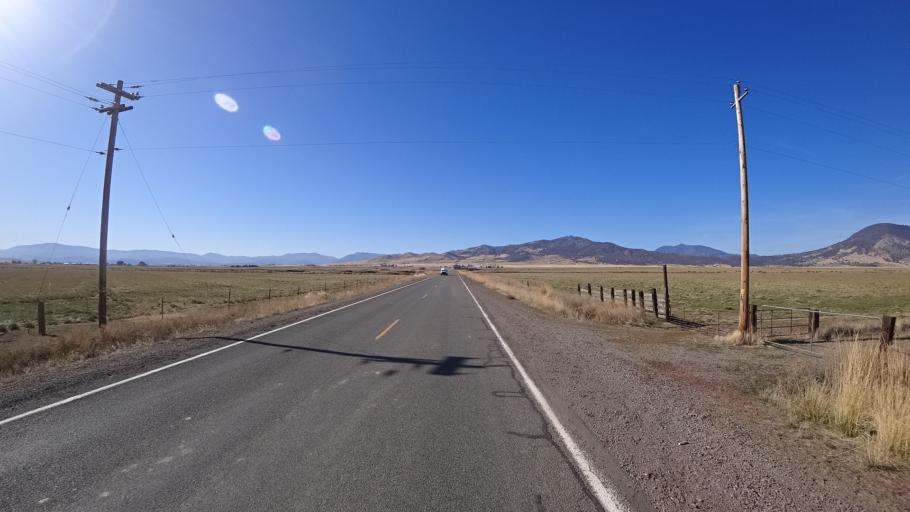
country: US
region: California
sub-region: Siskiyou County
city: Montague
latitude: 41.7938
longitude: -122.4593
